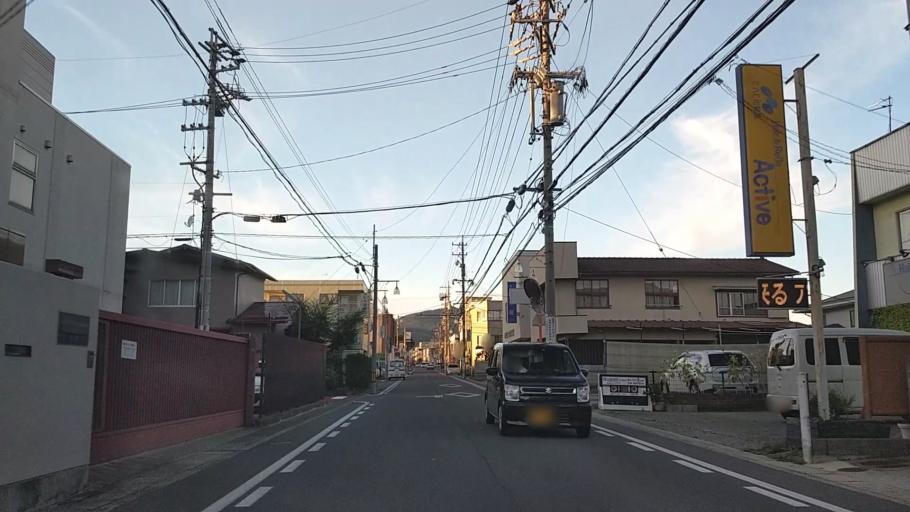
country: JP
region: Nagano
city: Nagano-shi
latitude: 36.6569
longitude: 138.2033
